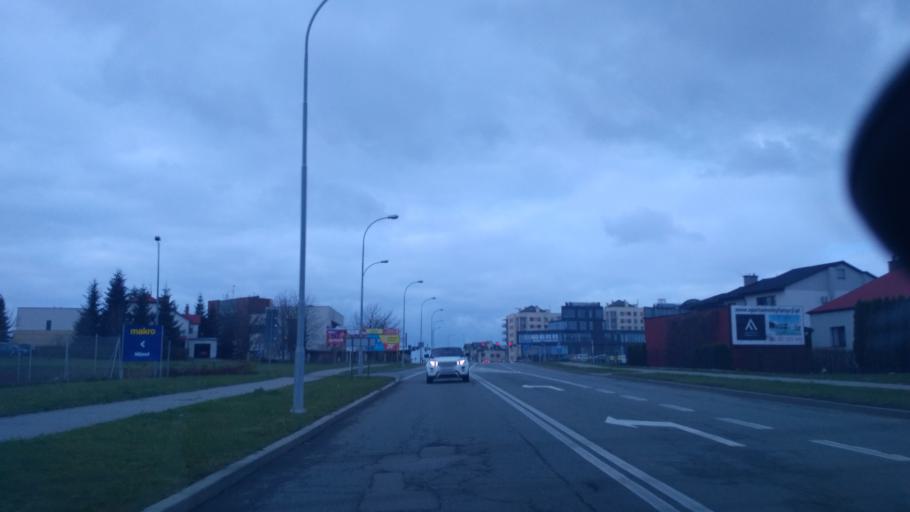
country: PL
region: Subcarpathian Voivodeship
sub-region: Rzeszow
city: Rzeszow
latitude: 50.0321
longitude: 22.0369
